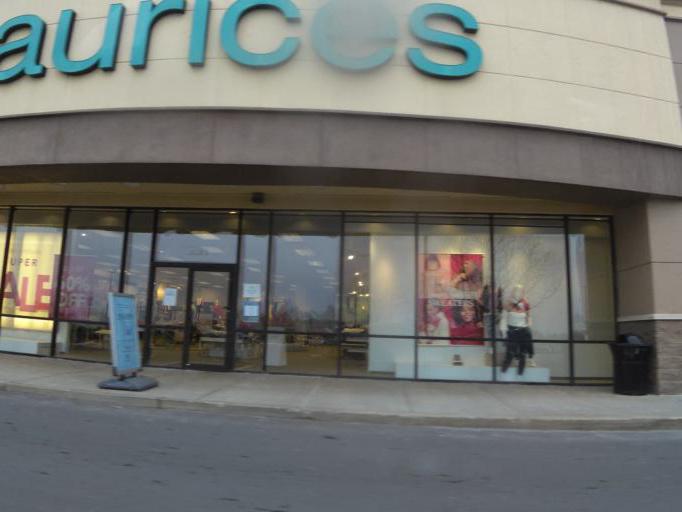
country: US
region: Missouri
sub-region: Marion County
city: Hannibal
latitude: 39.7237
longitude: -91.3996
